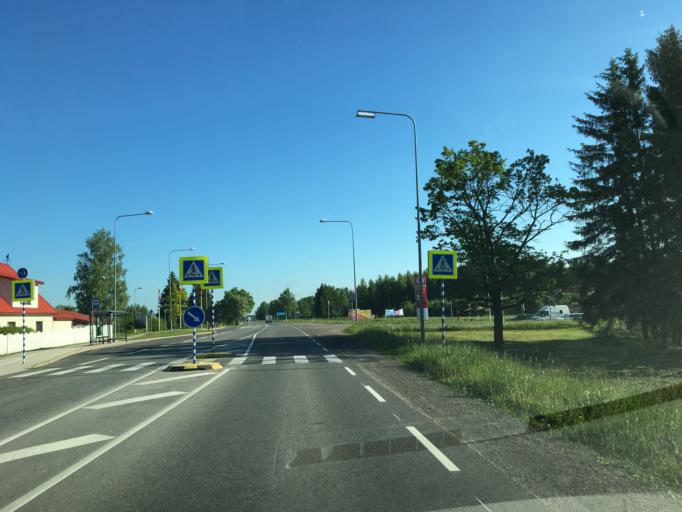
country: EE
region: Tartu
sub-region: Tartu linn
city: Tartu
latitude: 58.4060
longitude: 26.7084
